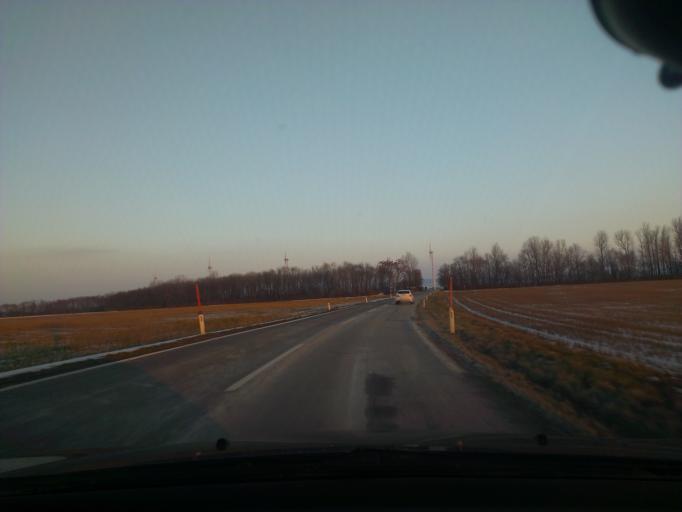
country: AT
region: Lower Austria
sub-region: Politischer Bezirk Baden
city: Mitterndorf an der Fischa
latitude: 47.9643
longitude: 16.4620
